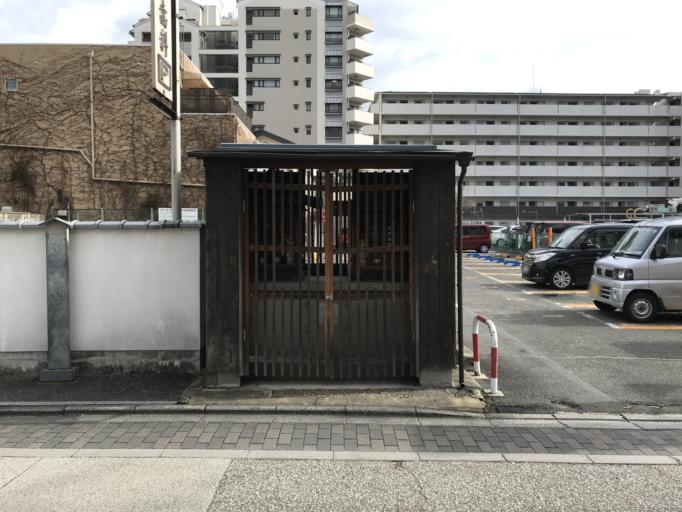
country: JP
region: Kyoto
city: Uji
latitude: 34.9314
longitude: 135.7619
